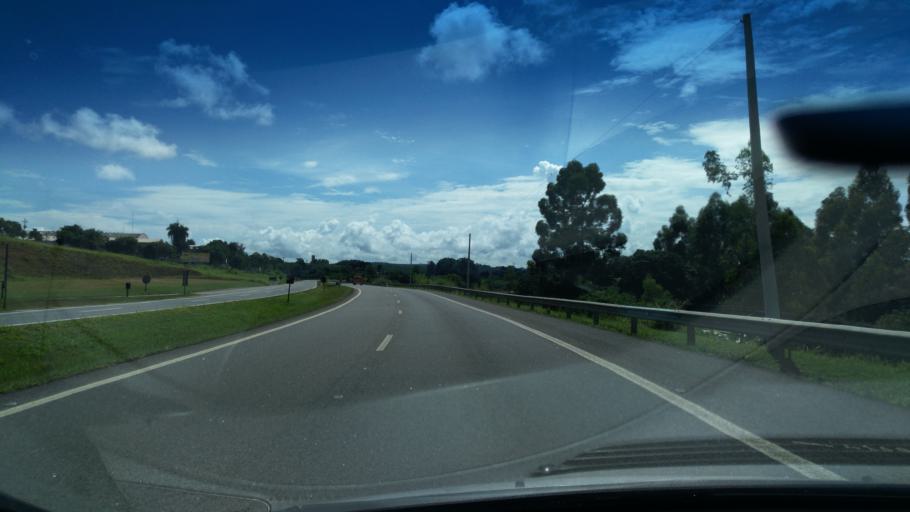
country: BR
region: Sao Paulo
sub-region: Santo Antonio Do Jardim
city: Espirito Santo do Pinhal
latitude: -22.2053
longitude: -46.7779
